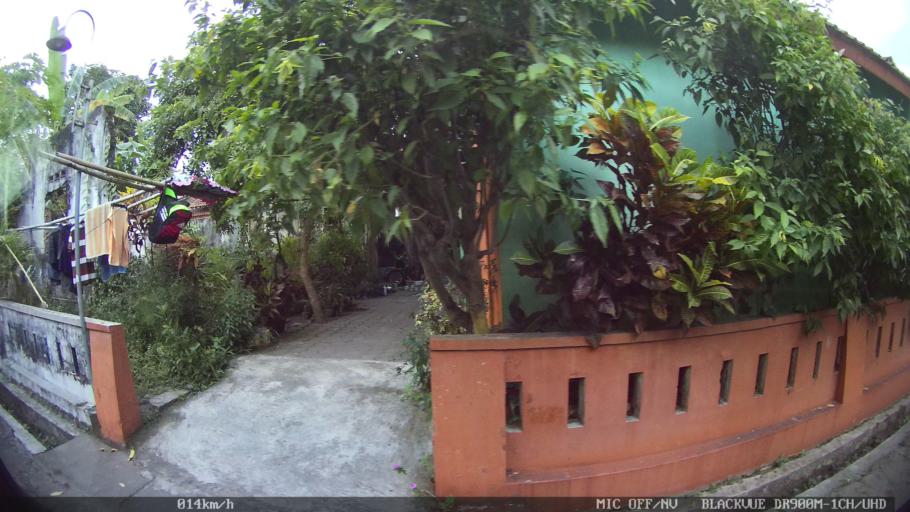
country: ID
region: Daerah Istimewa Yogyakarta
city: Kasihan
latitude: -7.8198
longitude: 110.3264
